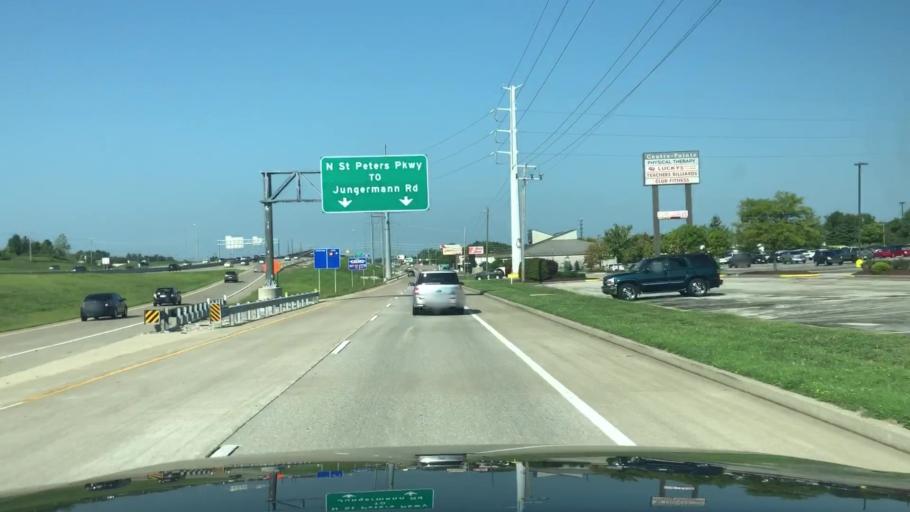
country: US
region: Missouri
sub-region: Saint Charles County
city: Saint Peters
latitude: 38.7486
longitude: -90.5860
